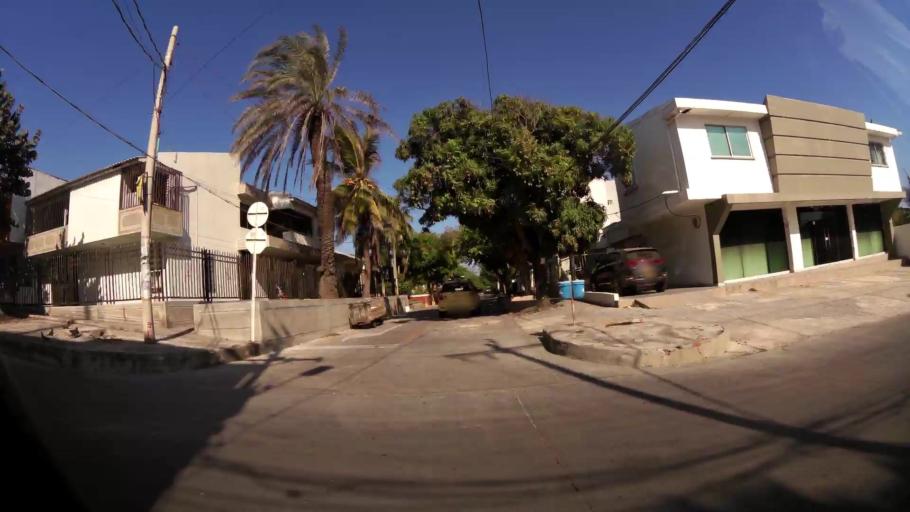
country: CO
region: Atlantico
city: Barranquilla
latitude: 11.0205
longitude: -74.8034
